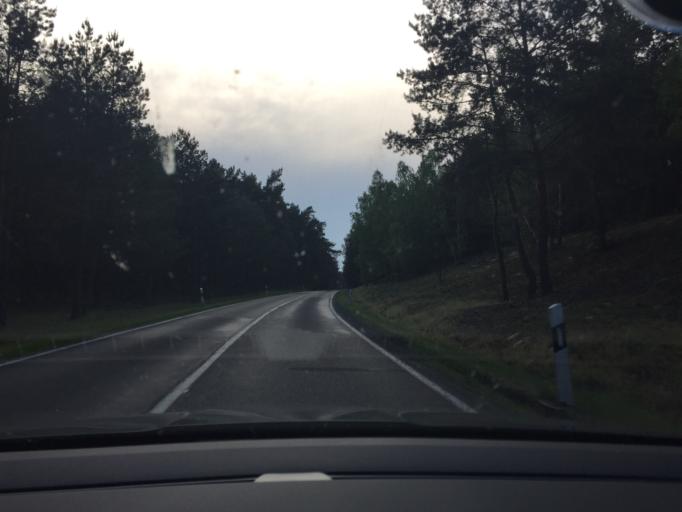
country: DE
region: Brandenburg
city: Treuenbrietzen
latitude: 52.1466
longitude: 12.9387
